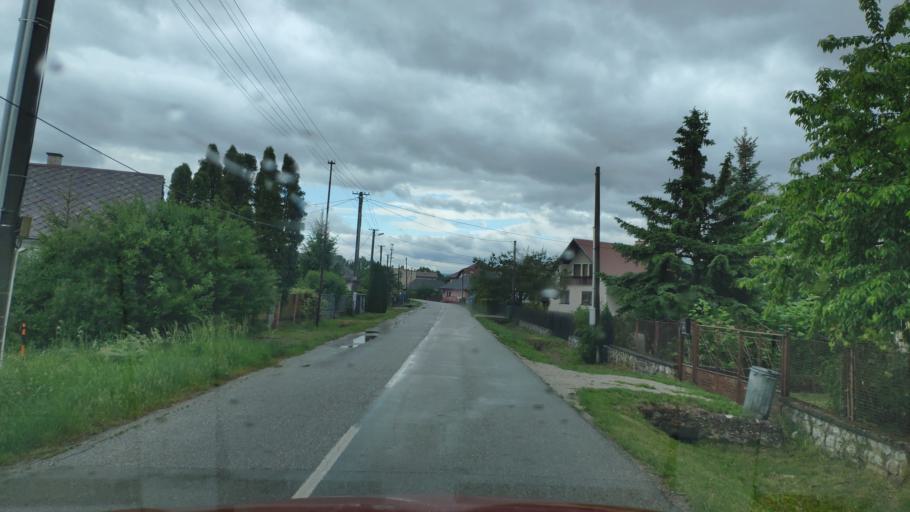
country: SK
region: Kosicky
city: Moldava nad Bodvou
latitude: 48.5426
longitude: 21.0478
